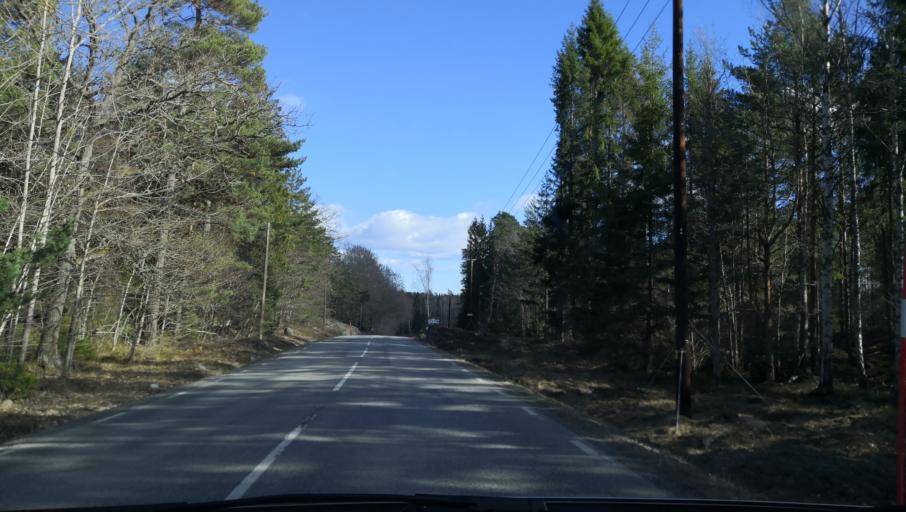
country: SE
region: Stockholm
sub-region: Varmdo Kommun
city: Hemmesta
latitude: 59.3608
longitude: 18.5375
